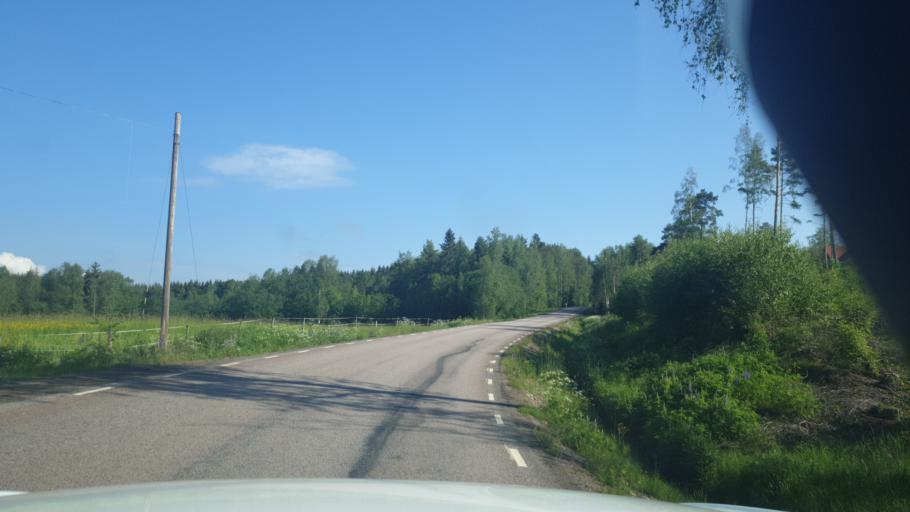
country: SE
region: Vaermland
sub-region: Eda Kommun
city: Charlottenberg
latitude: 59.7672
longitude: 12.2080
